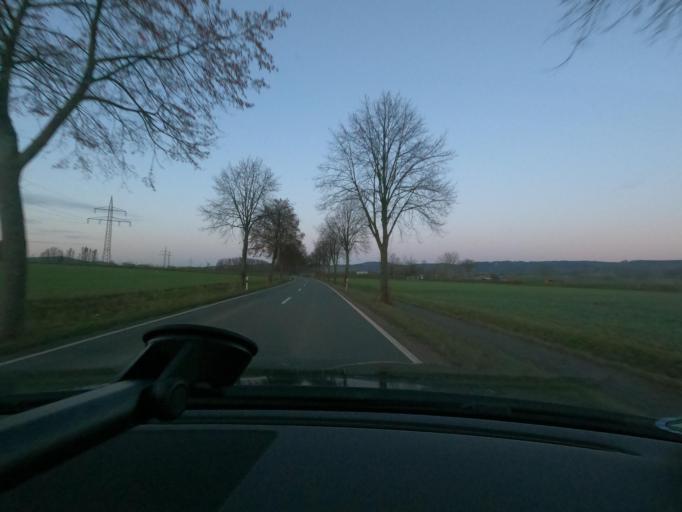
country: DE
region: Lower Saxony
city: Badenhausen
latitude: 51.7731
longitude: 10.1898
